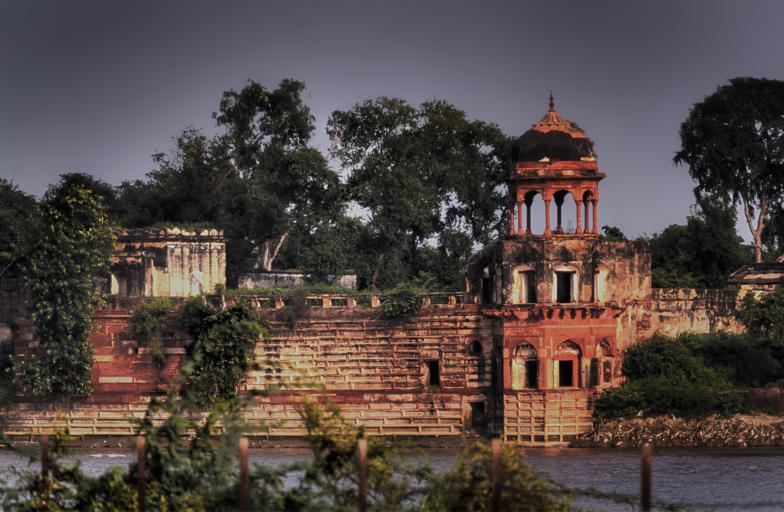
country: IN
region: Uttar Pradesh
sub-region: Agra
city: Agra
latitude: 27.1785
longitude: 78.0416
